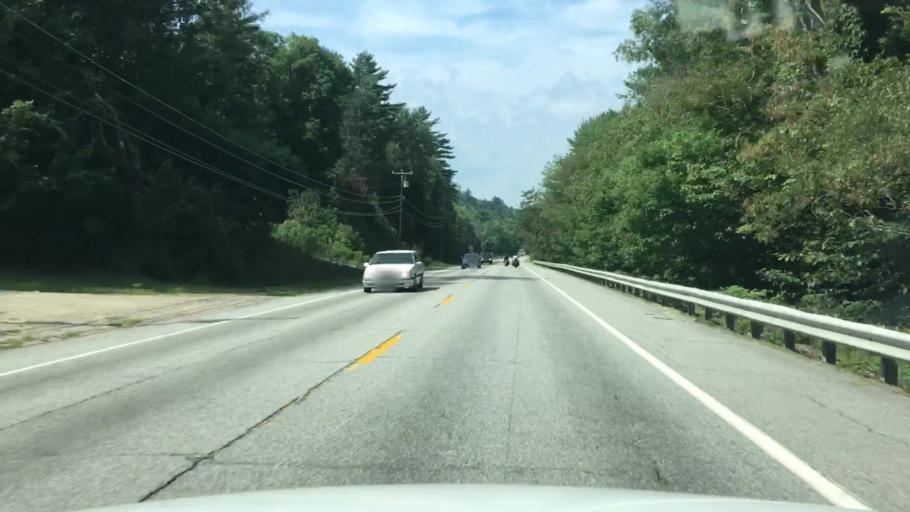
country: US
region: Maine
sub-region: Oxford County
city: Peru
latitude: 44.5130
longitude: -70.4162
